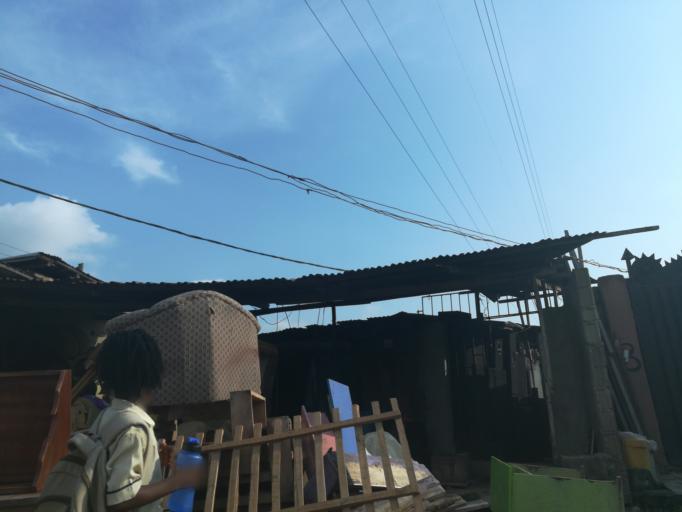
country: NG
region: Lagos
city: Ojota
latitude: 6.5924
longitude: 3.3996
